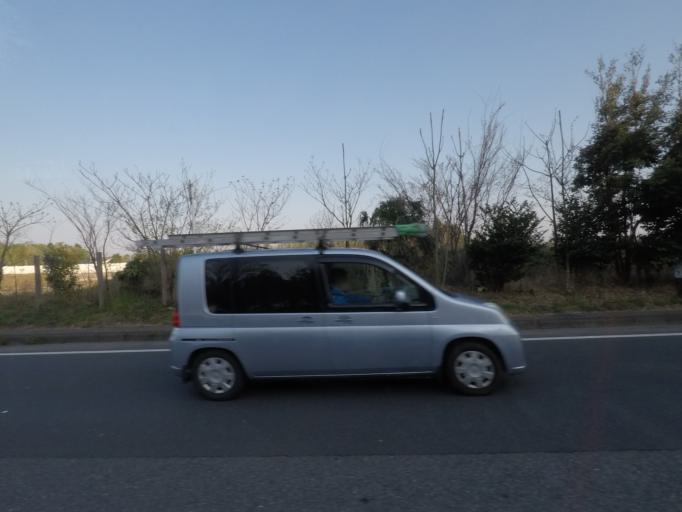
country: JP
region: Chiba
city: Yotsukaido
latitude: 35.6443
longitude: 140.1813
